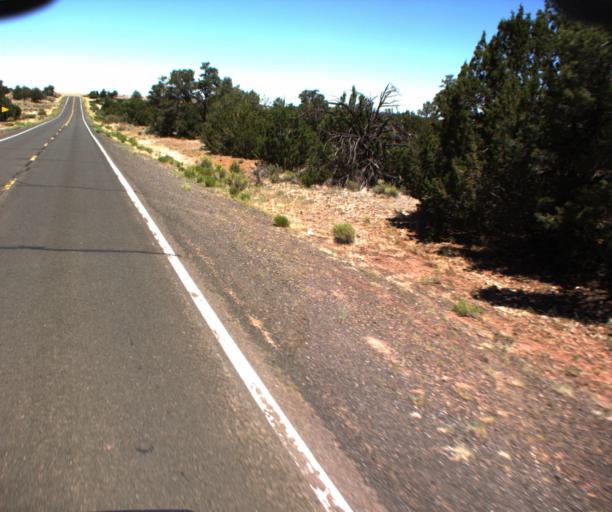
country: US
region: Arizona
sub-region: Coconino County
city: LeChee
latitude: 34.7156
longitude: -111.0915
